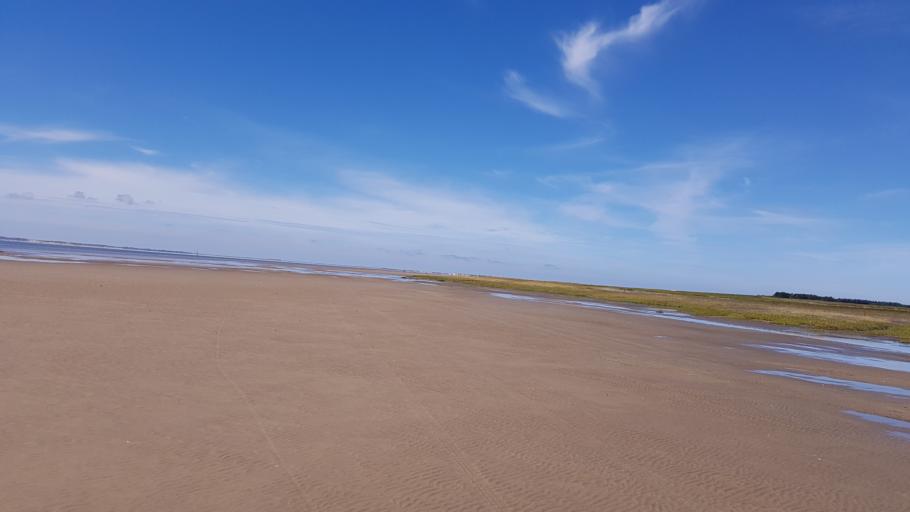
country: DE
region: Schleswig-Holstein
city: List
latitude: 55.0748
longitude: 8.5451
